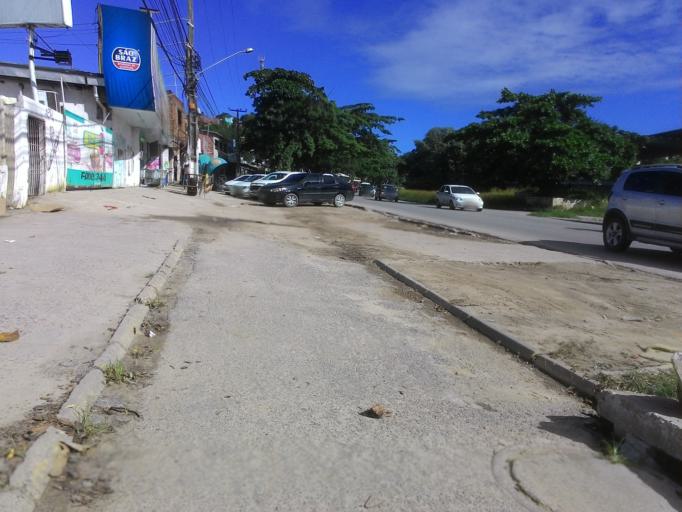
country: BR
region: Pernambuco
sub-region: Olinda
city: Olinda
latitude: -7.9828
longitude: -34.8556
